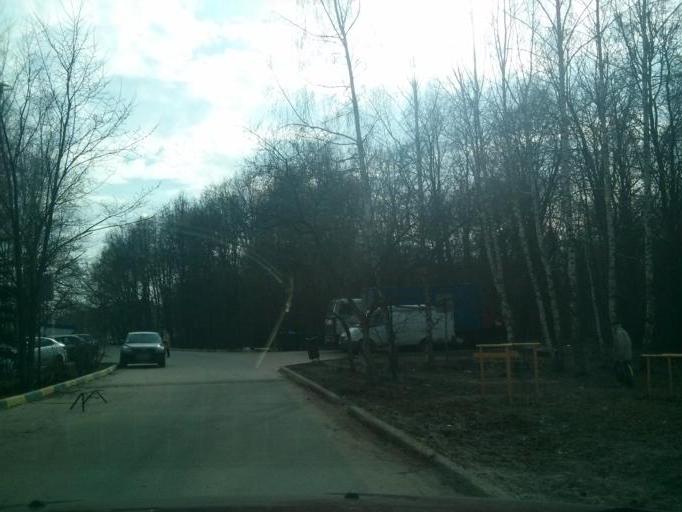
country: RU
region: Nizjnij Novgorod
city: Nizhniy Novgorod
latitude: 56.2643
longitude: 44.0122
